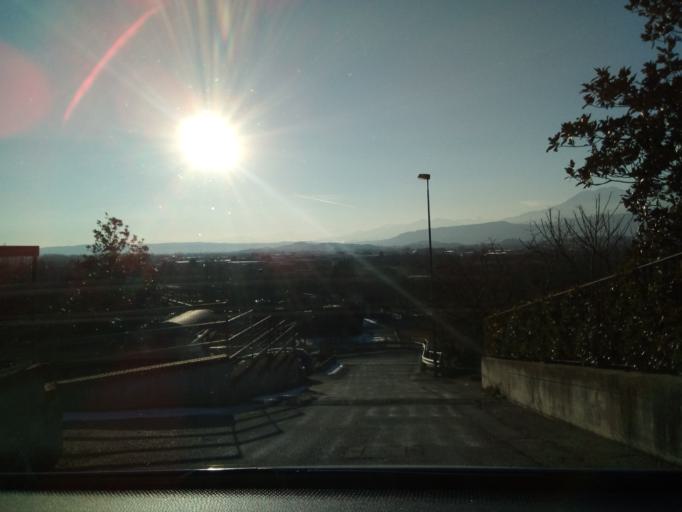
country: IT
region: Piedmont
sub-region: Provincia di Torino
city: Burolo
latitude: 45.4770
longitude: 7.9359
